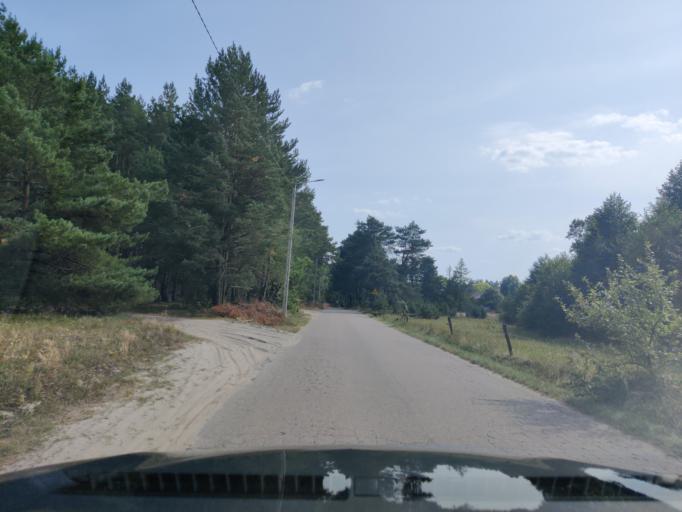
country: PL
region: Masovian Voivodeship
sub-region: Powiat makowski
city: Rozan
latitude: 52.8526
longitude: 21.4564
